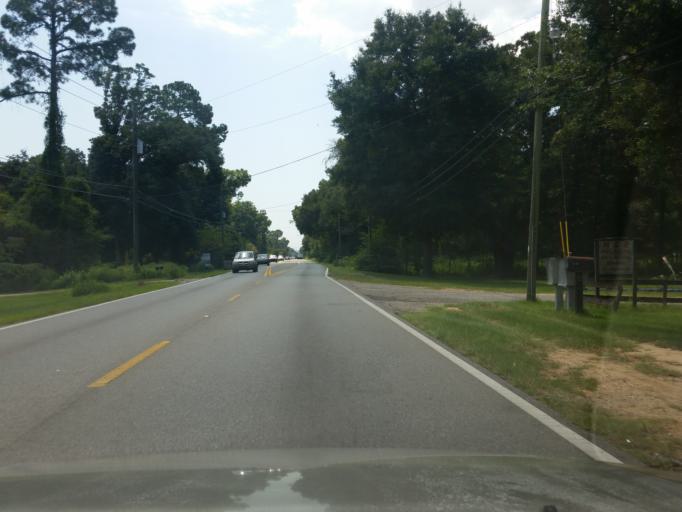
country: US
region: Florida
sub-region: Escambia County
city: Ensley
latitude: 30.5116
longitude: -87.2626
